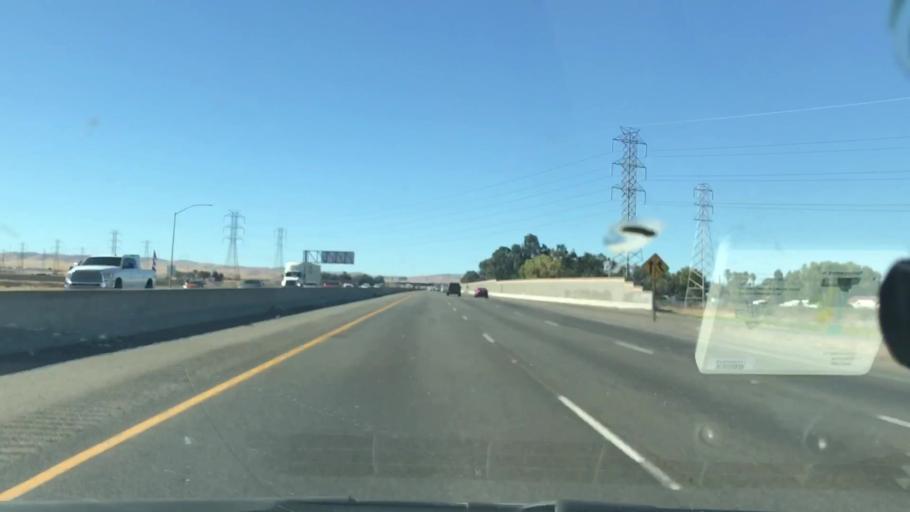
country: US
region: California
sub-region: San Joaquin County
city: Mountain House
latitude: 37.7395
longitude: -121.5018
